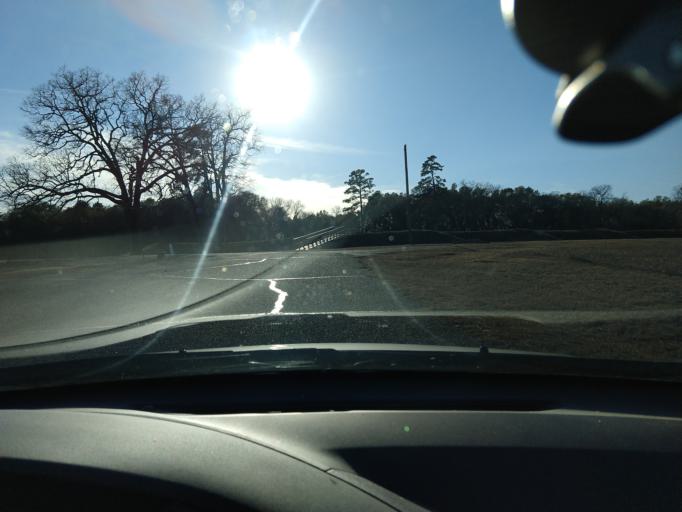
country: US
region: Georgia
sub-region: Macon County
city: Oglethorpe
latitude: 32.1925
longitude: -84.1315
